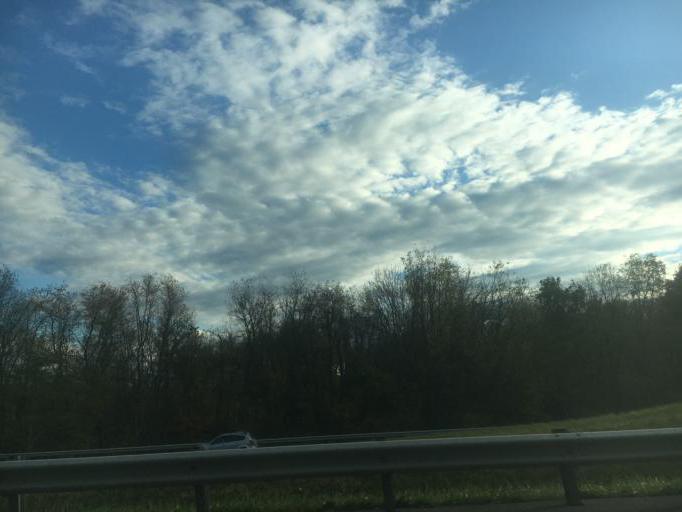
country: US
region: Virginia
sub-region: Washington County
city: Emory
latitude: 36.7695
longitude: -81.8085
